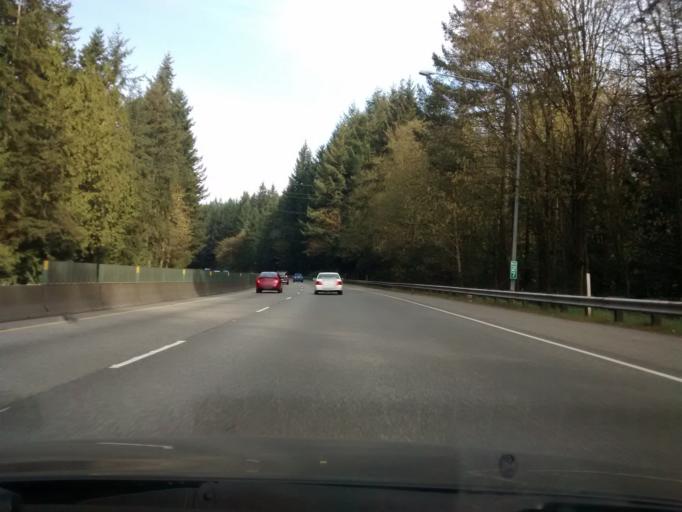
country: US
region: Washington
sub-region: Kitsap County
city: Navy Yard City
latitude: 47.5261
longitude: -122.6617
